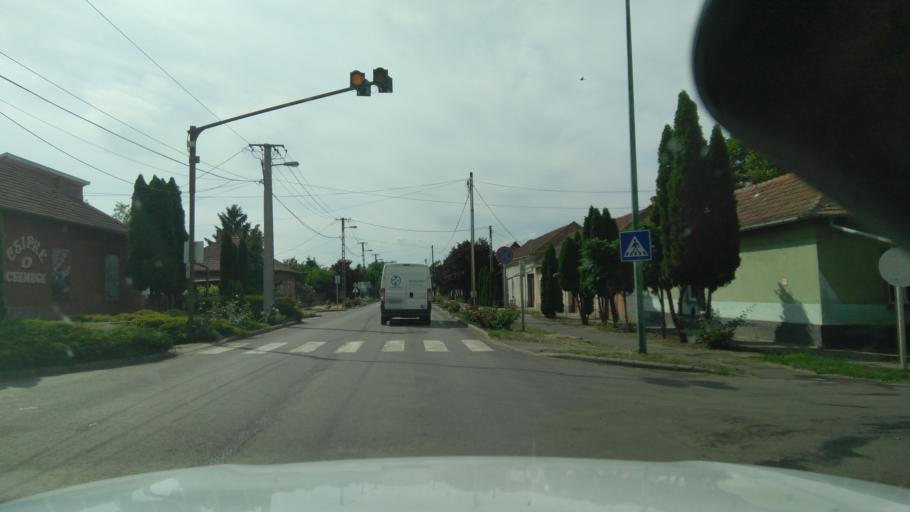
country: HU
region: Bekes
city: Medgyesegyhaza
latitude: 46.5007
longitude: 21.0230
